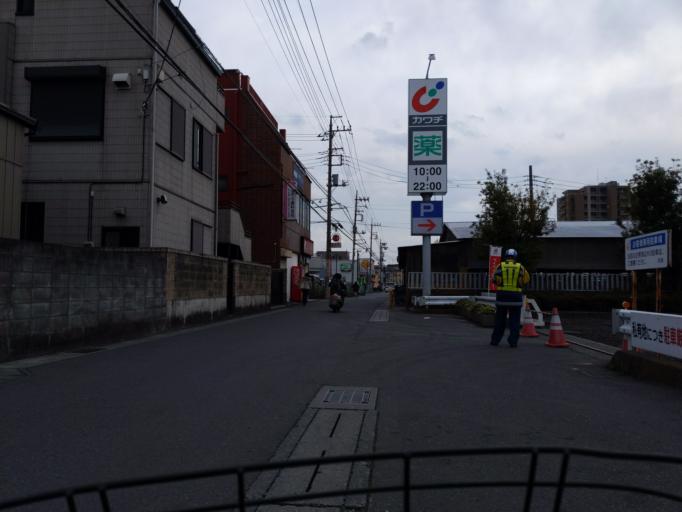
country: JP
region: Saitama
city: Koshigaya
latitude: 35.8541
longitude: 139.7943
